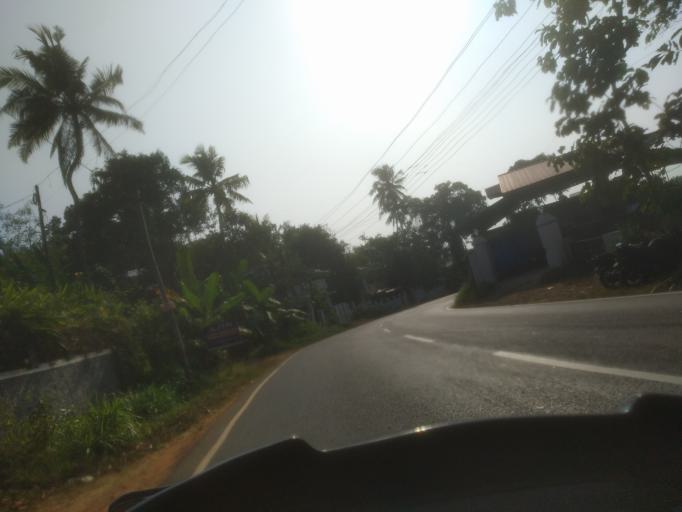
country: IN
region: Kerala
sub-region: Ernakulam
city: Piravam
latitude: 9.8307
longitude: 76.5077
